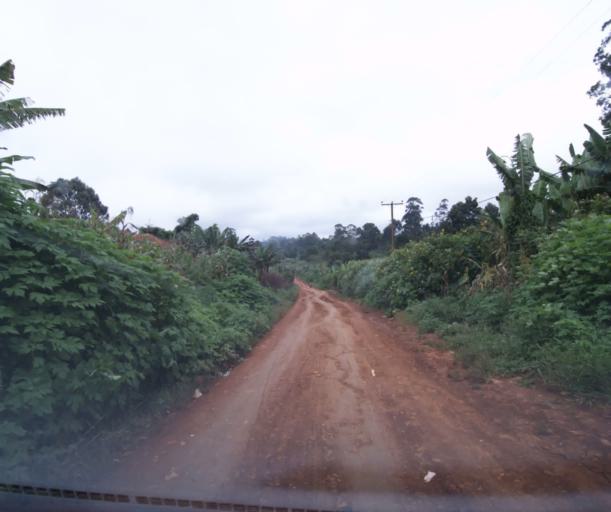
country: CM
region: West
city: Dschang
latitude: 5.5074
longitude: 9.9943
